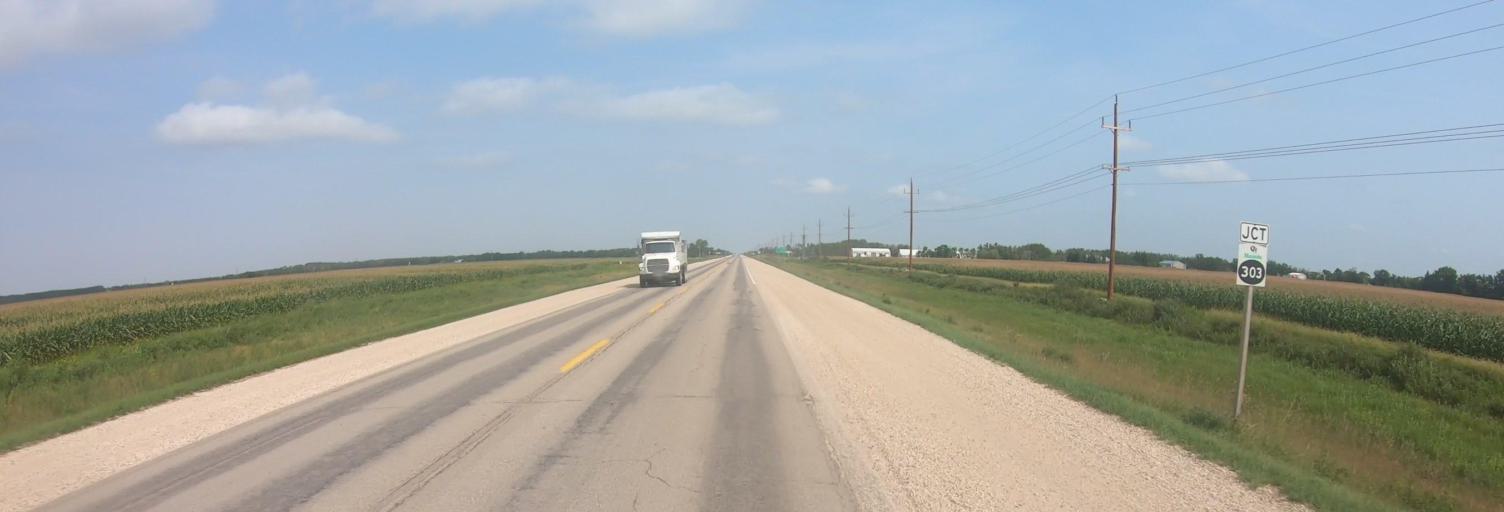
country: CA
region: Manitoba
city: Steinbach
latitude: 49.4697
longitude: -96.6911
